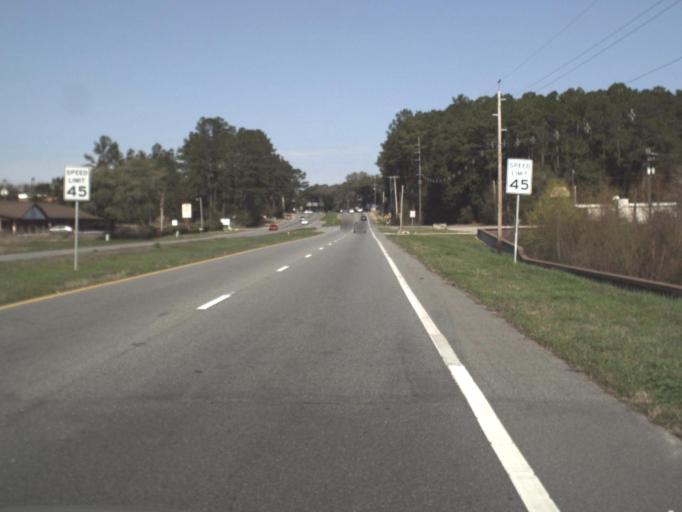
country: US
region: Florida
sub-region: Gadsden County
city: Midway
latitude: 30.5289
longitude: -84.3586
